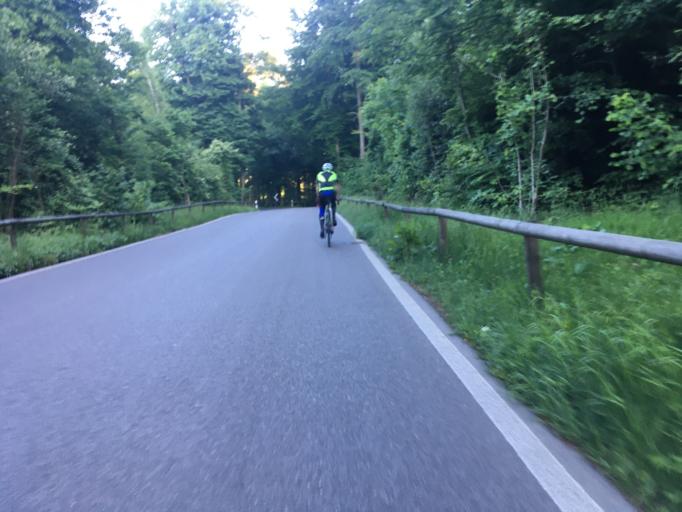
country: CH
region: Zurich
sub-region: Bezirk Meilen
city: Kuesnacht / Schiedhalden
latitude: 47.3284
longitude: 8.5910
